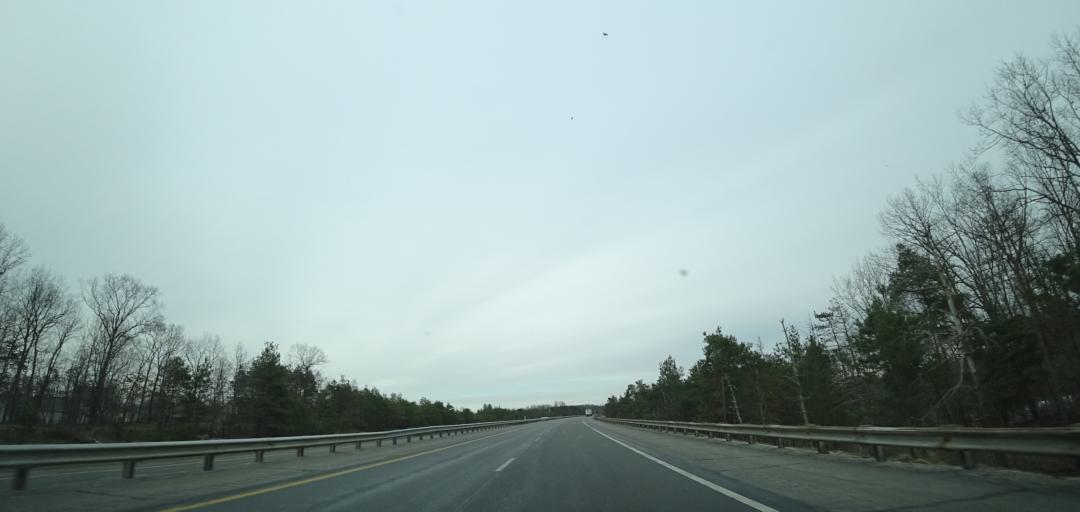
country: US
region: Ohio
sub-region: Mahoning County
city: Austintown
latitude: 41.0788
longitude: -80.8025
